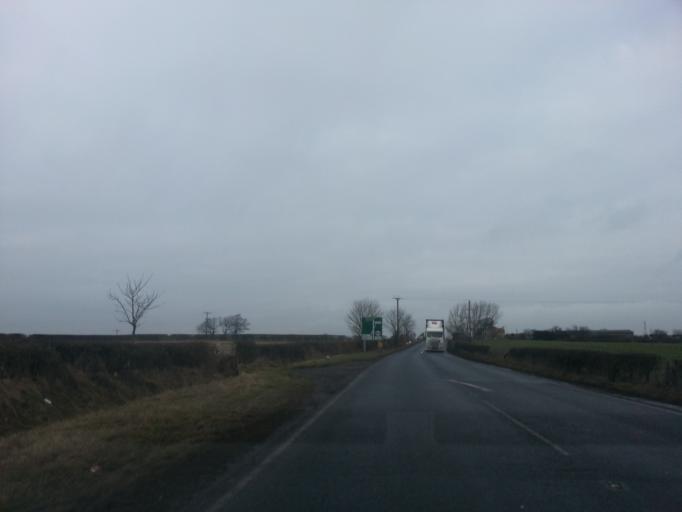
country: GB
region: England
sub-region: Darlington
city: Summerhouse
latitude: 54.6046
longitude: -1.6776
